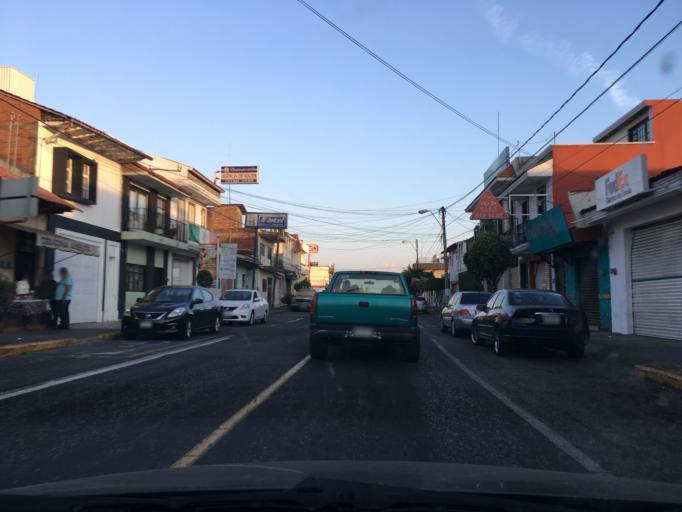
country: MX
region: Michoacan
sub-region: Uruapan
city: Uruapan
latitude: 19.4164
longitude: -102.0629
